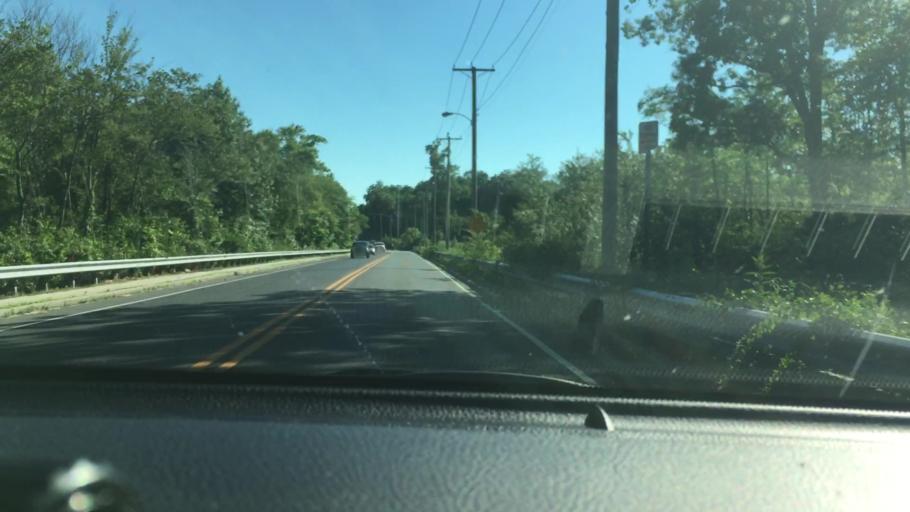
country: US
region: New Jersey
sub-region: Cumberland County
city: Millville
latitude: 39.4017
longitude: -75.0517
